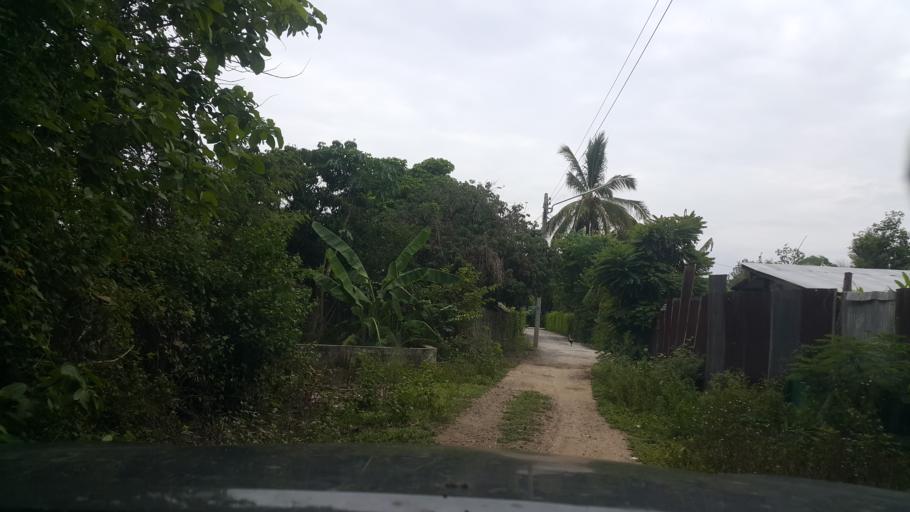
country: TH
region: Chiang Mai
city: Hang Dong
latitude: 18.6826
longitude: 98.8929
